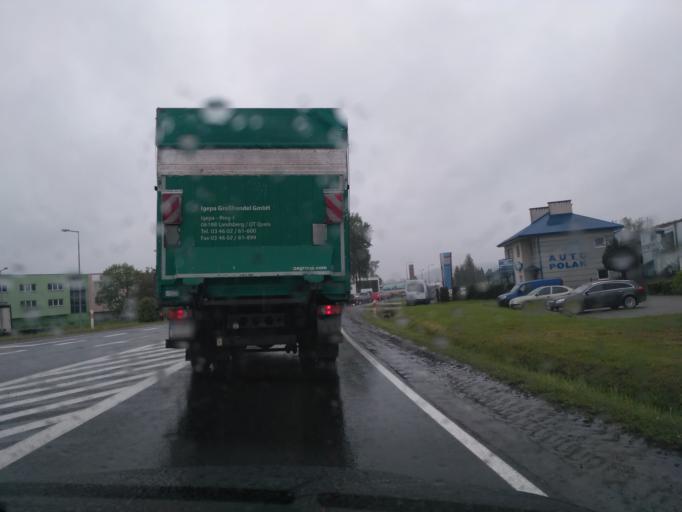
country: PL
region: Lesser Poland Voivodeship
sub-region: Powiat gorlicki
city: Kobylanka
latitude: 49.6846
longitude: 21.1906
